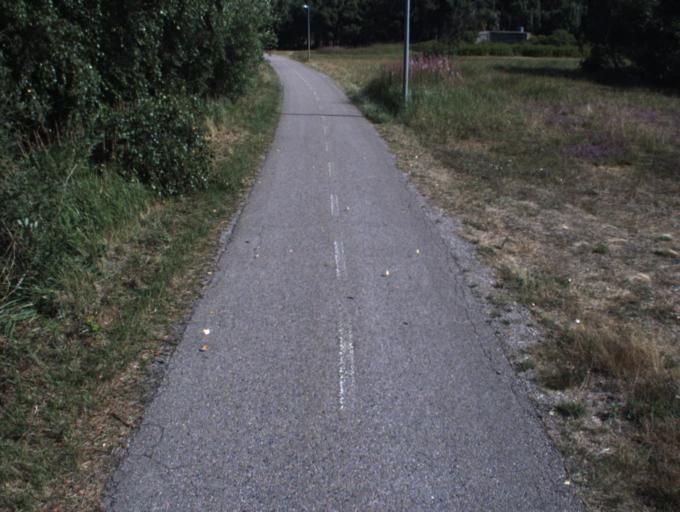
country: SE
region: Skane
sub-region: Helsingborg
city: Rydeback
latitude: 55.9811
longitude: 12.7545
